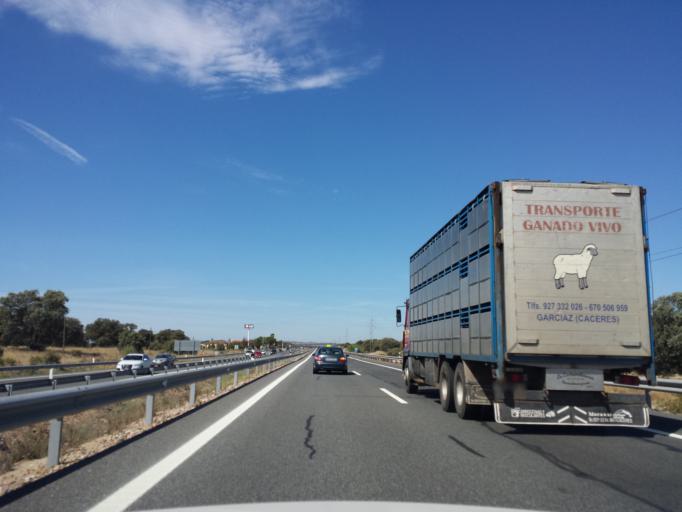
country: ES
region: Castille-La Mancha
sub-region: Province of Toledo
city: Alcanizo
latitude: 39.9191
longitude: -5.0529
